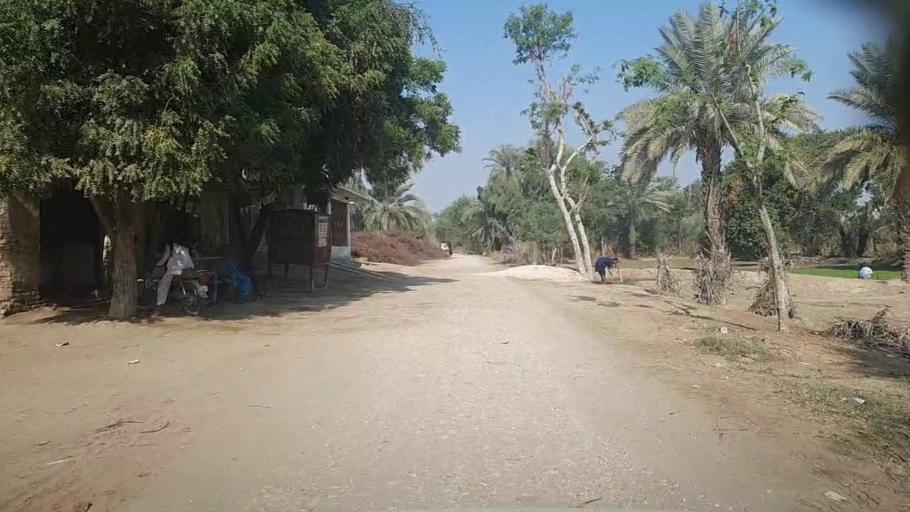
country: PK
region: Sindh
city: Kandiari
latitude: 26.9385
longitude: 68.5316
